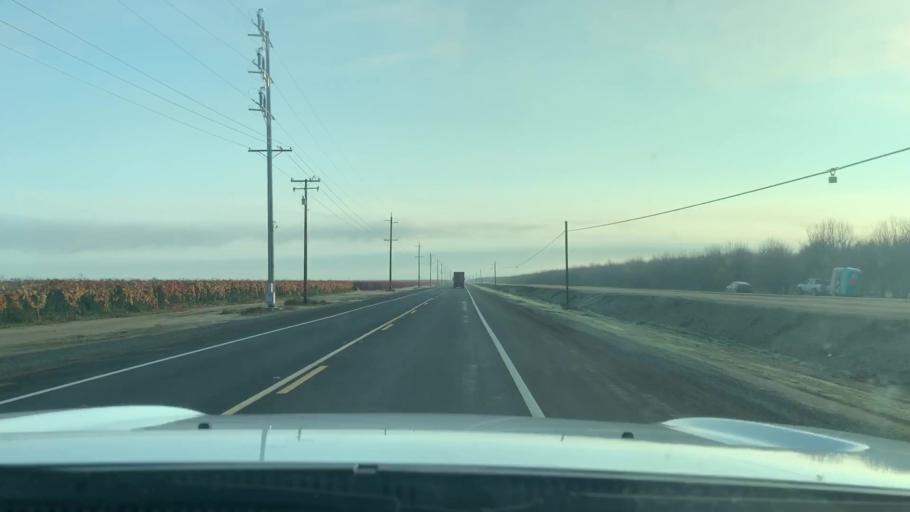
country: US
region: California
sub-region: Kern County
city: Wasco
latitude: 35.6017
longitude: -119.2742
